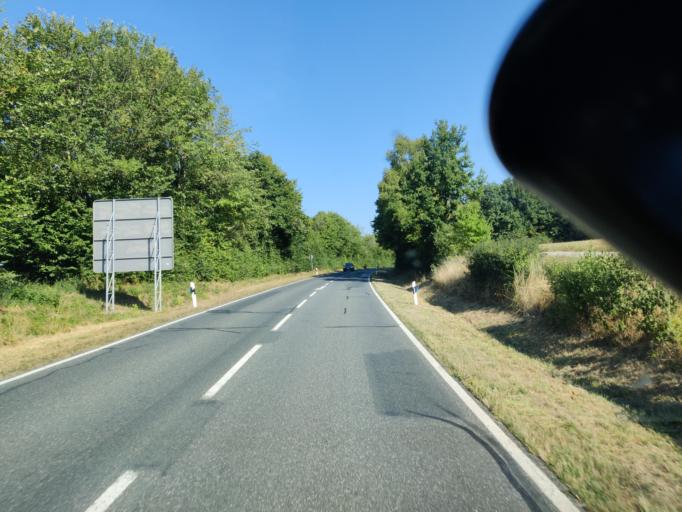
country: DE
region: Bavaria
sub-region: Regierungsbezirk Mittelfranken
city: Hilpoltstein
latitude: 49.1721
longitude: 11.2282
